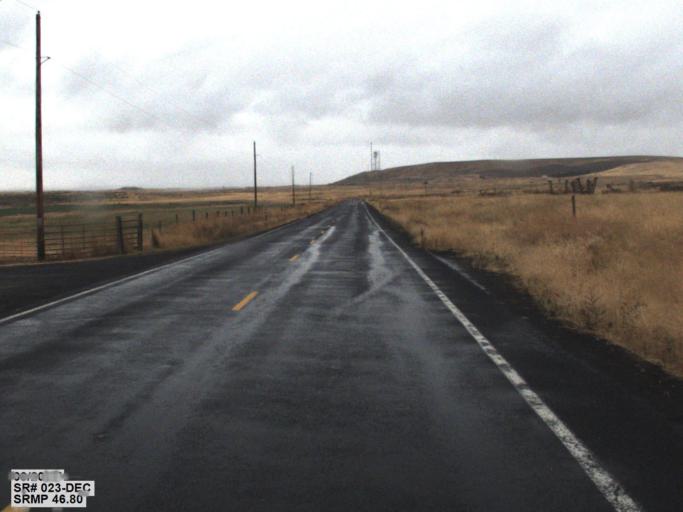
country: US
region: Washington
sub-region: Lincoln County
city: Davenport
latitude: 47.3386
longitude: -118.0035
